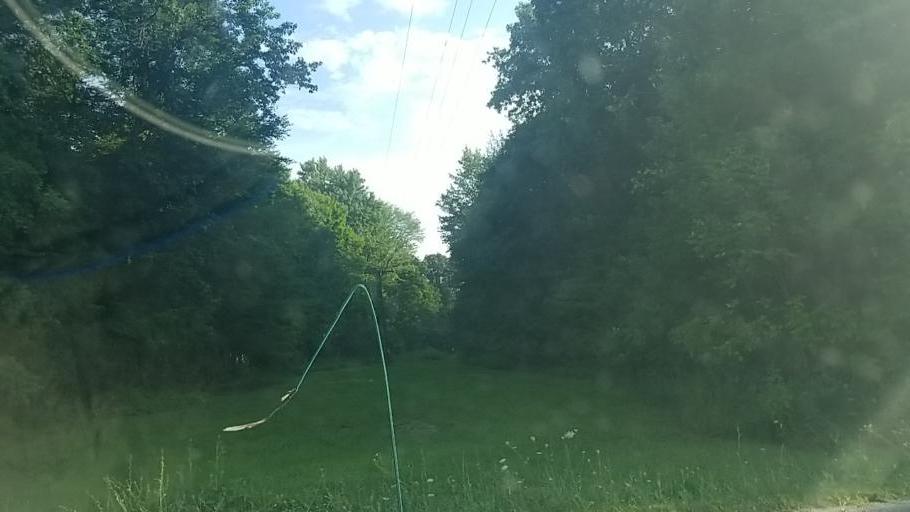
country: US
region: Ohio
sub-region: Ashland County
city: Ashland
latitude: 40.8711
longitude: -82.1927
